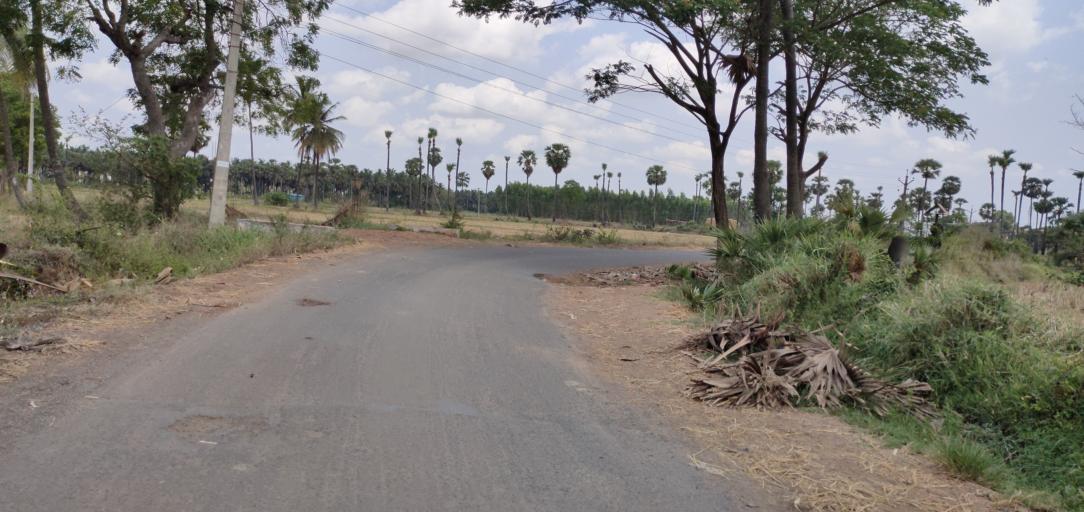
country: IN
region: Andhra Pradesh
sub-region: West Godavari
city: Tadepallegudem
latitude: 16.8509
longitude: 81.4940
